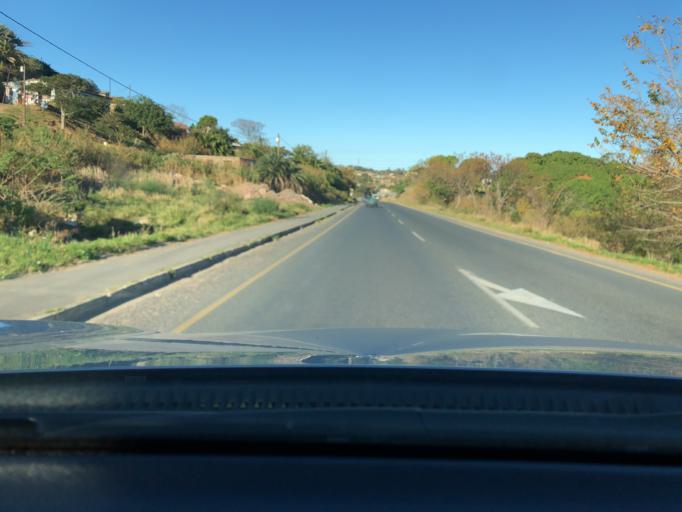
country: ZA
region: KwaZulu-Natal
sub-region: eThekwini Metropolitan Municipality
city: Umkomaas
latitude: -30.0362
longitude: 30.8604
